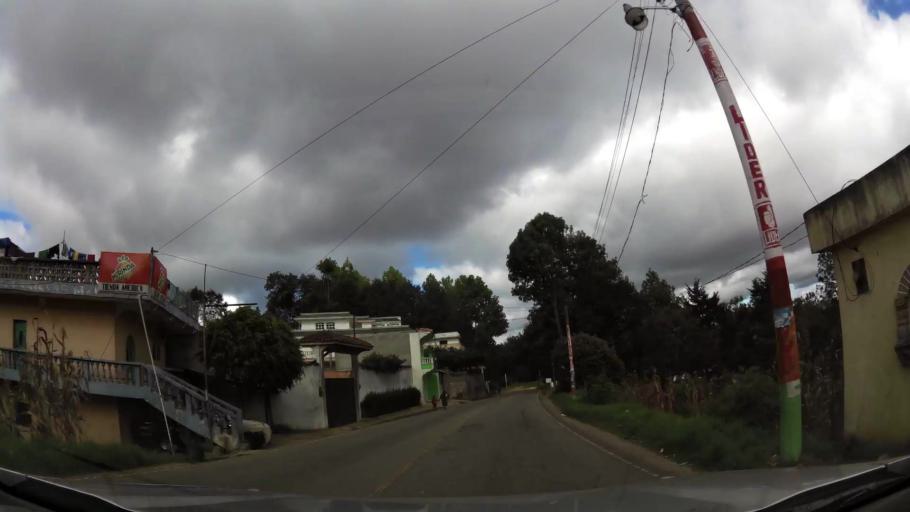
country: GT
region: Quiche
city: Chichicastenango
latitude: 14.8969
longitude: -91.1160
